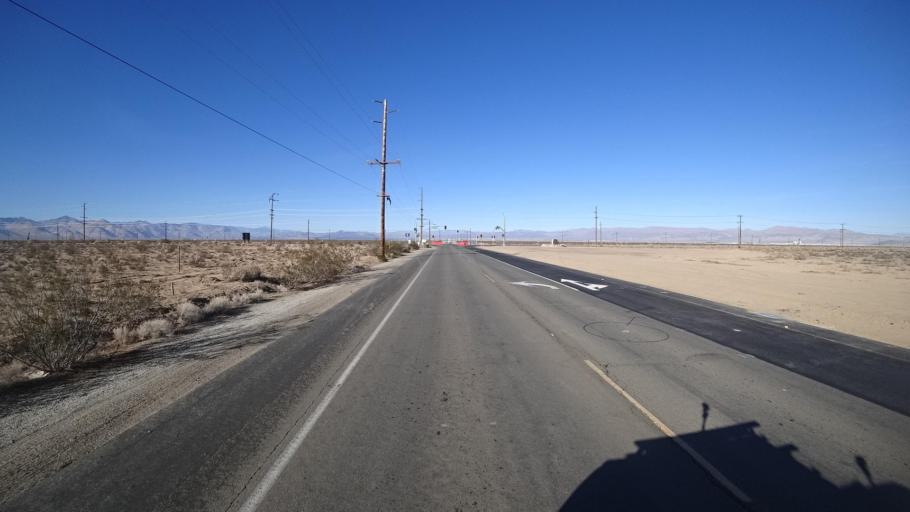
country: US
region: California
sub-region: Kern County
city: China Lake Acres
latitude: 35.6506
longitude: -117.7231
